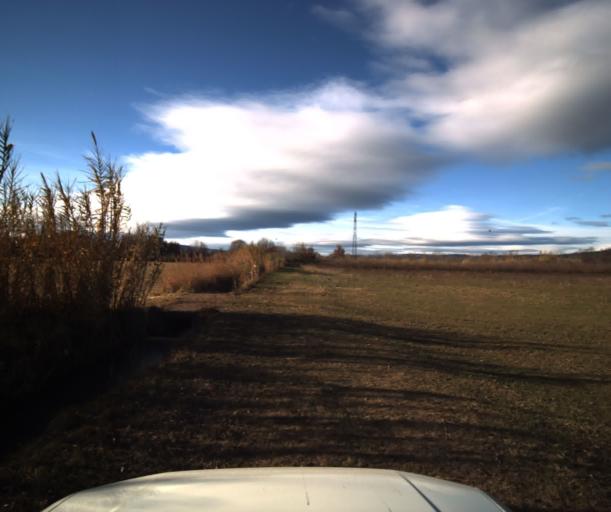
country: FR
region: Provence-Alpes-Cote d'Azur
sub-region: Departement du Vaucluse
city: Pertuis
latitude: 43.6790
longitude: 5.4708
